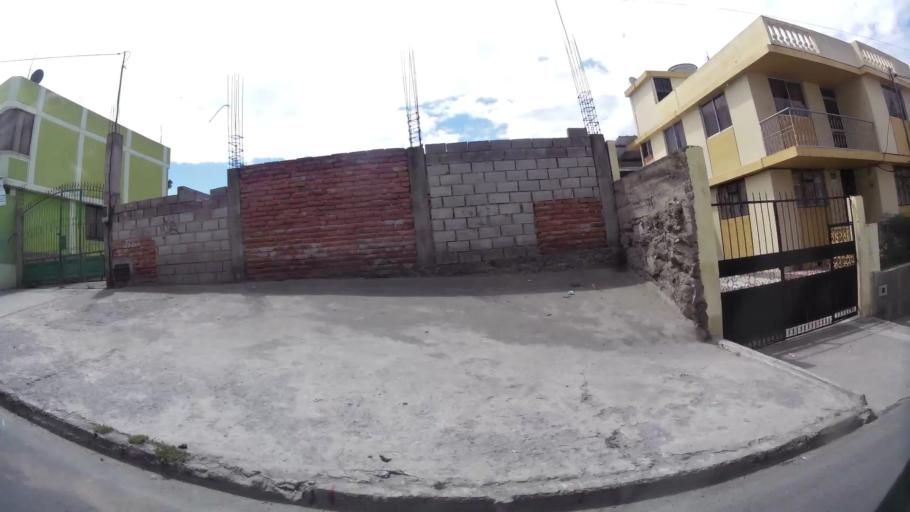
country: EC
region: Pichincha
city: Quito
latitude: -0.0634
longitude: -78.4283
